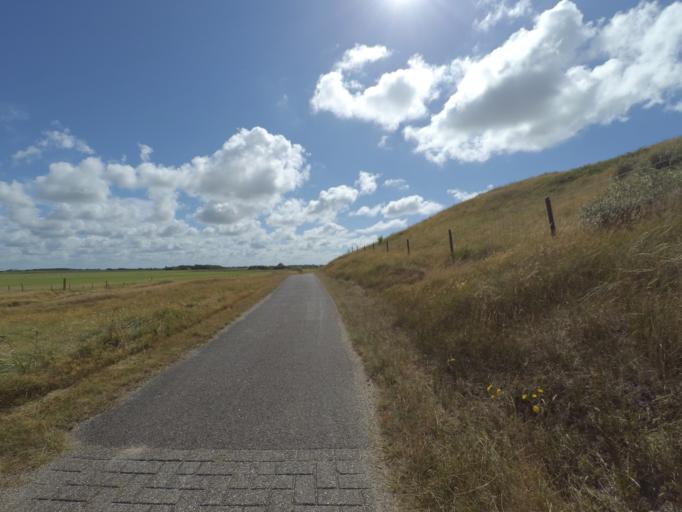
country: NL
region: North Holland
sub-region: Gemeente Texel
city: Den Burg
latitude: 53.1383
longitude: 4.8252
